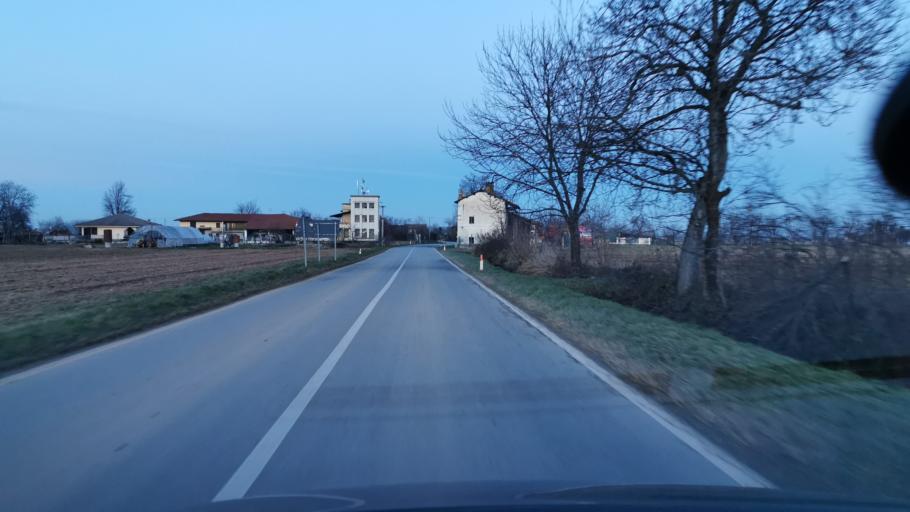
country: IT
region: Piedmont
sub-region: Provincia di Cuneo
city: Caraglio
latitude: 44.4325
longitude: 7.4526
